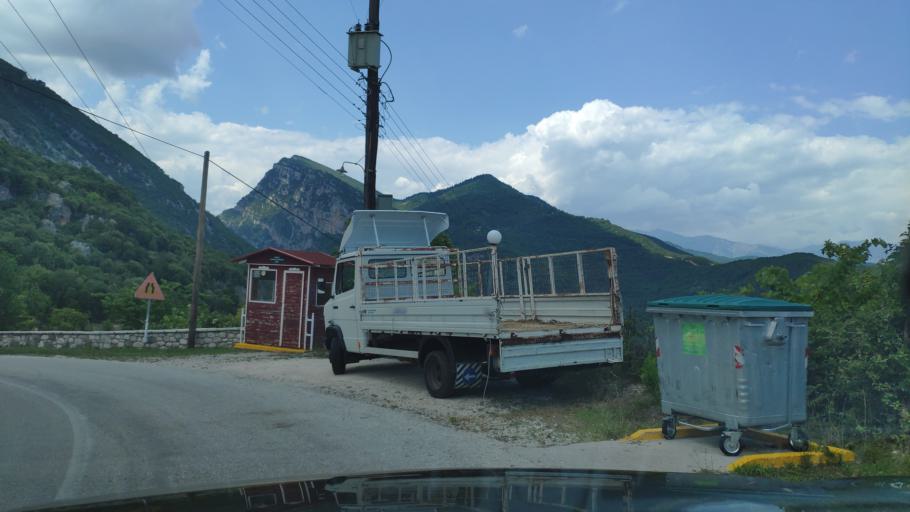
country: GR
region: Epirus
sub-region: Nomos Artas
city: Agios Dimitrios
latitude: 39.4586
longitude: 21.0240
